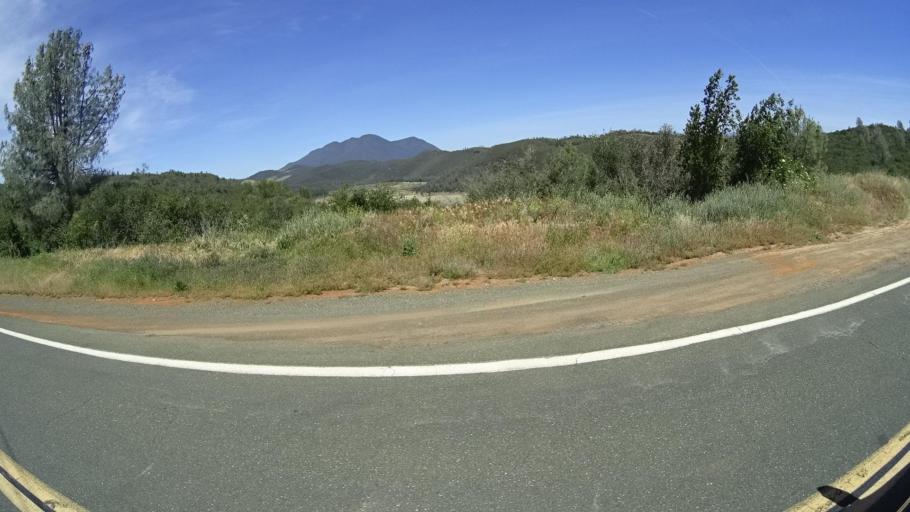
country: US
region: California
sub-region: Lake County
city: Clearlake
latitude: 38.9234
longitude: -122.6620
